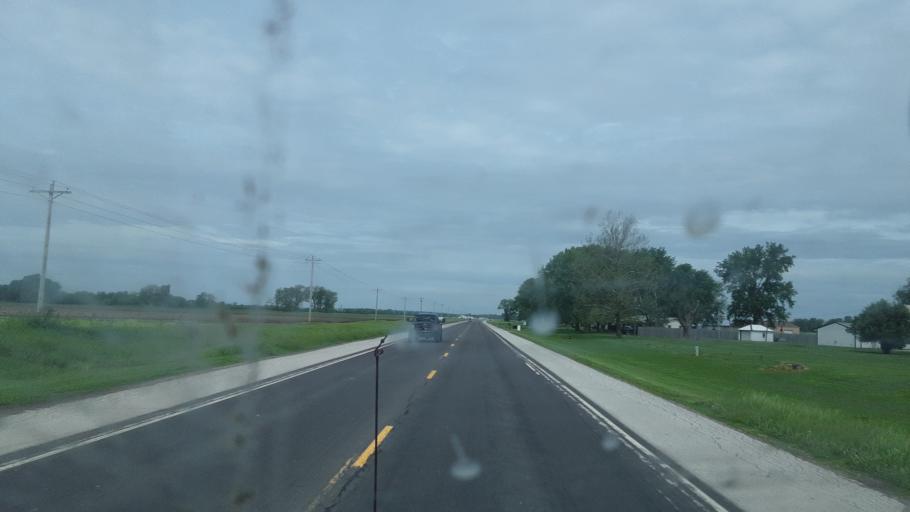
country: US
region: Illinois
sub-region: Hancock County
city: Warsaw
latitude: 40.3715
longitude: -91.4799
